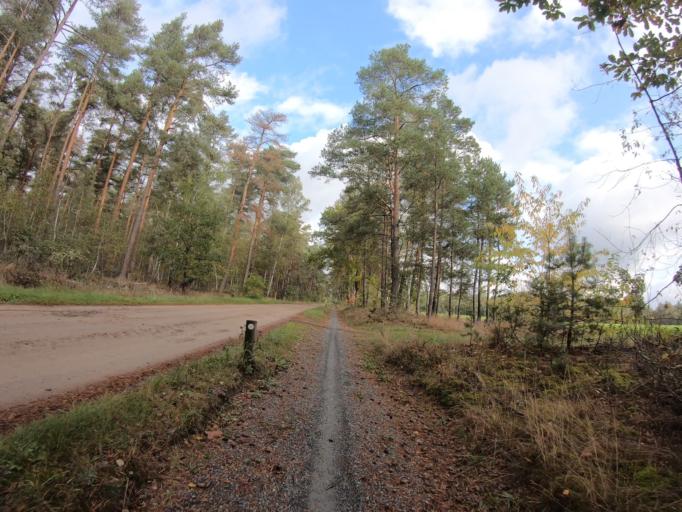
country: DE
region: Lower Saxony
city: Wesendorf
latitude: 52.5763
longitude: 10.5686
